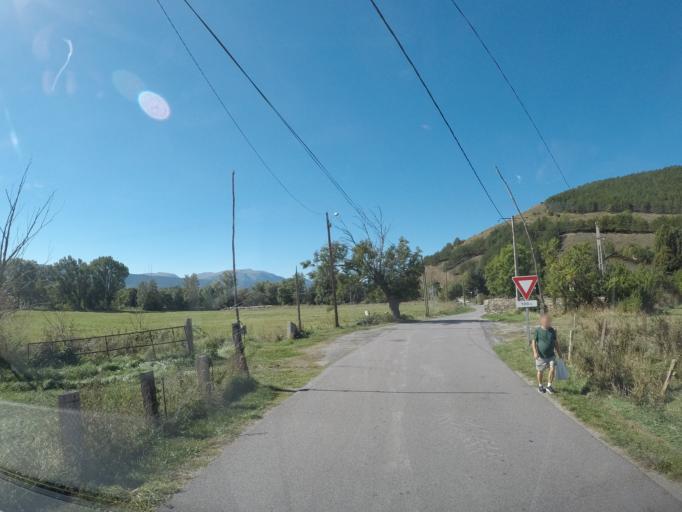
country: ES
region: Catalonia
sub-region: Provincia de Girona
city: Llivia
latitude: 42.4664
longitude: 1.9939
